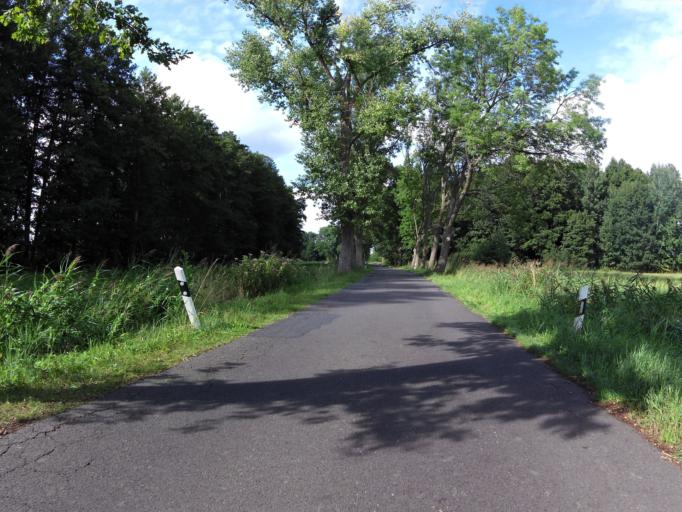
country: DE
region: Brandenburg
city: Storkow
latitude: 52.2378
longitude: 13.9331
